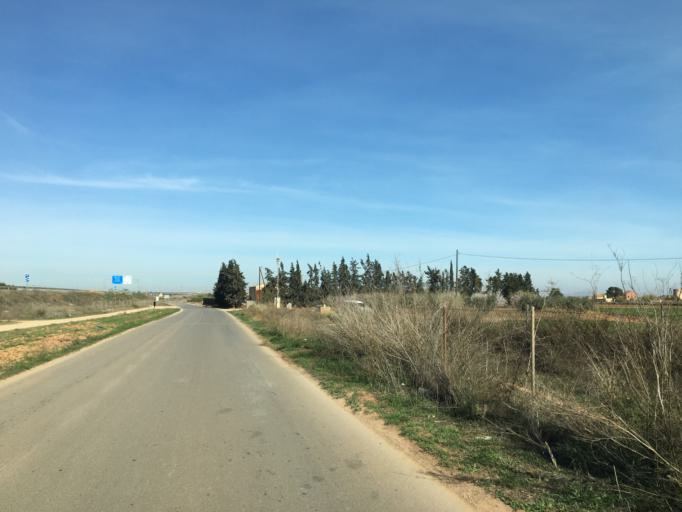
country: ES
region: Murcia
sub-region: Murcia
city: Cartagena
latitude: 37.6559
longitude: -1.0238
